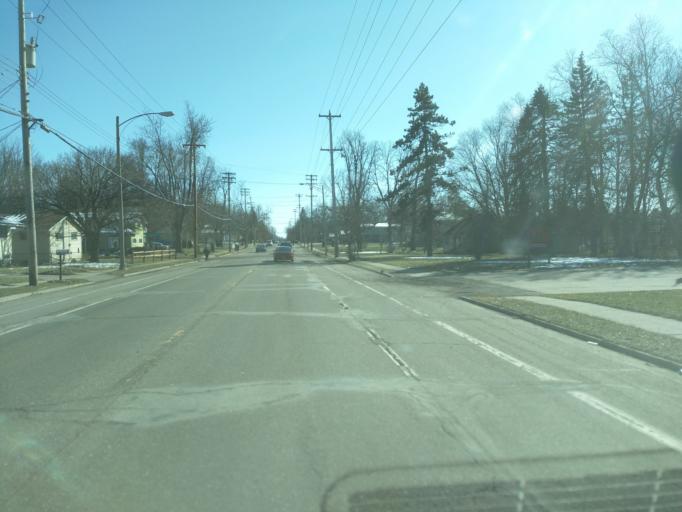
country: US
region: Michigan
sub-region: Ingham County
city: Lansing
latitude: 42.6947
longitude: -84.5823
